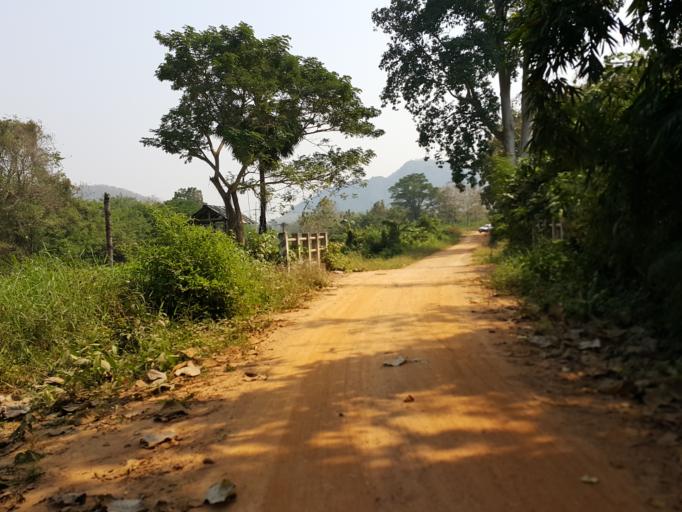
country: TH
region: Sukhothai
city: Thung Saliam
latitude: 17.3345
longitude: 99.4886
